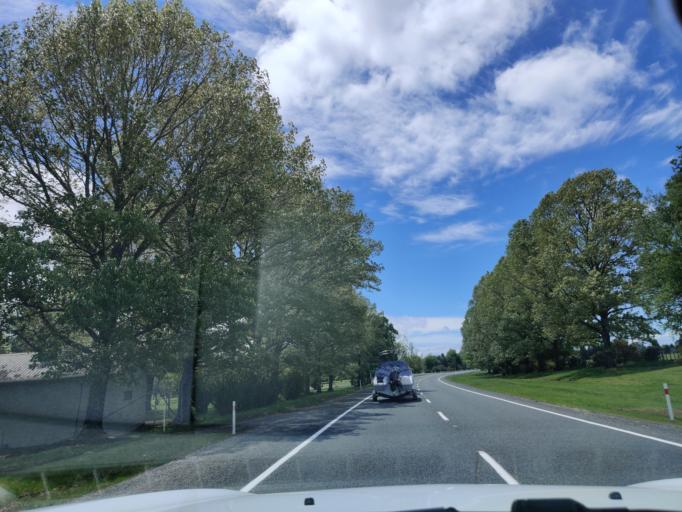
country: NZ
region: Waikato
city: Turangi
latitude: -38.9989
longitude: 175.8041
